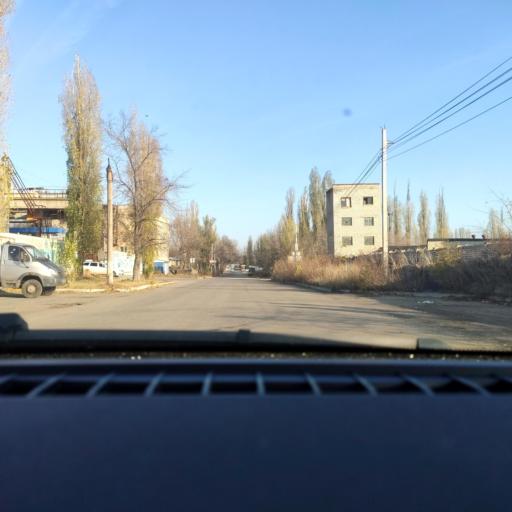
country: RU
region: Voronezj
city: Voronezh
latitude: 51.6474
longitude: 39.2872
